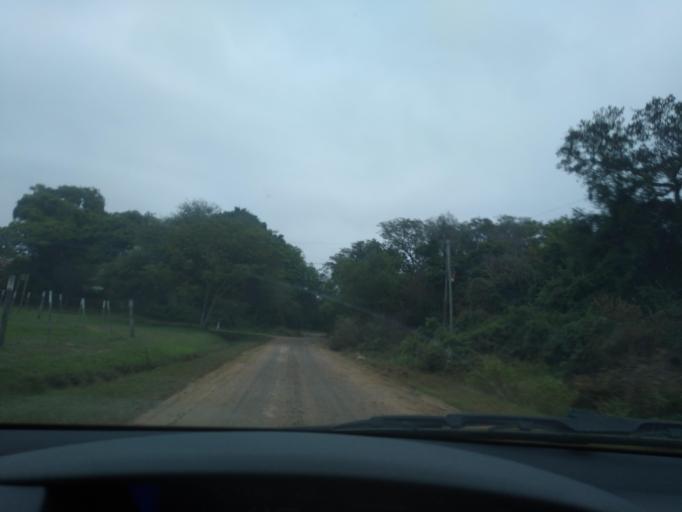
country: AR
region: Chaco
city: Colonia Benitez
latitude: -27.3337
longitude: -58.9649
